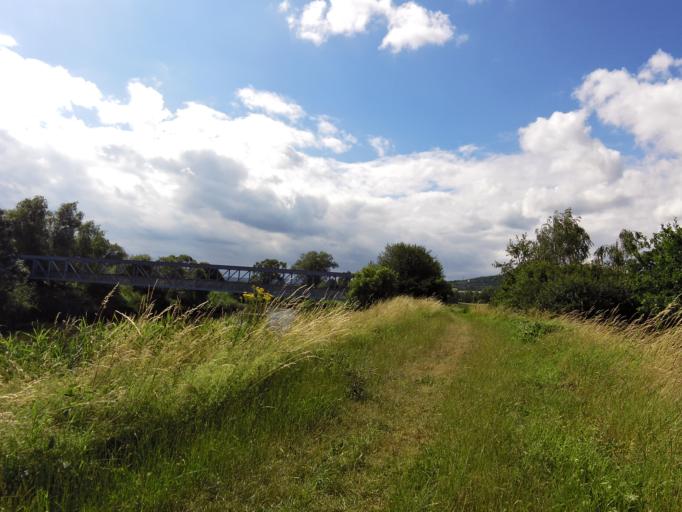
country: DE
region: Hesse
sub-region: Regierungsbezirk Kassel
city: Herleshausen
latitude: 50.9990
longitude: 10.1893
